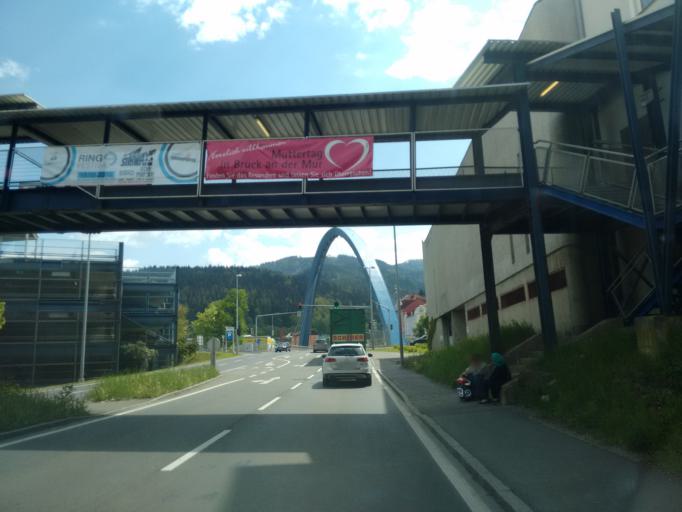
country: AT
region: Styria
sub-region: Politischer Bezirk Bruck-Muerzzuschlag
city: Bruck an der Mur
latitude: 47.4105
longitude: 15.2739
